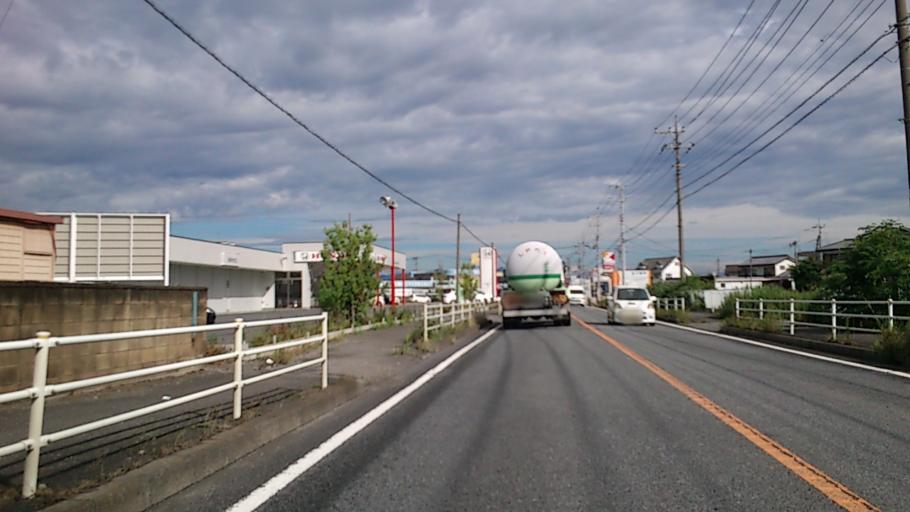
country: JP
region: Saitama
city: Honjo
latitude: 36.2380
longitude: 139.2056
